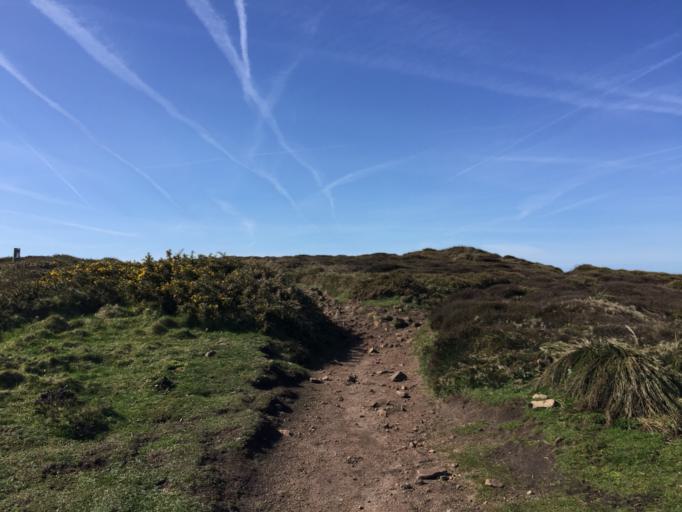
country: JE
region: St Helier
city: Saint Helier
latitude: 49.2486
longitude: -2.2510
